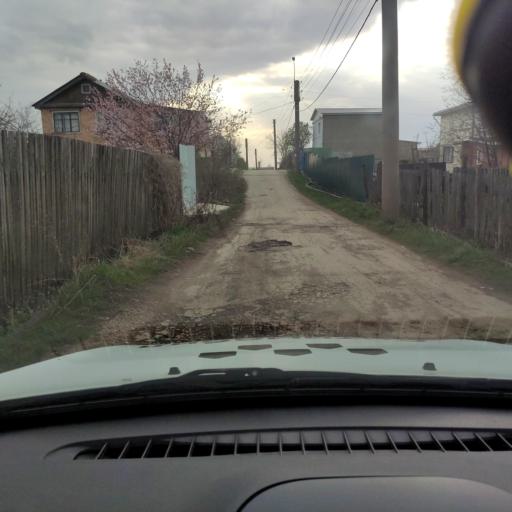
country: RU
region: Samara
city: Mezhdurechensk
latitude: 53.2447
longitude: 49.1500
